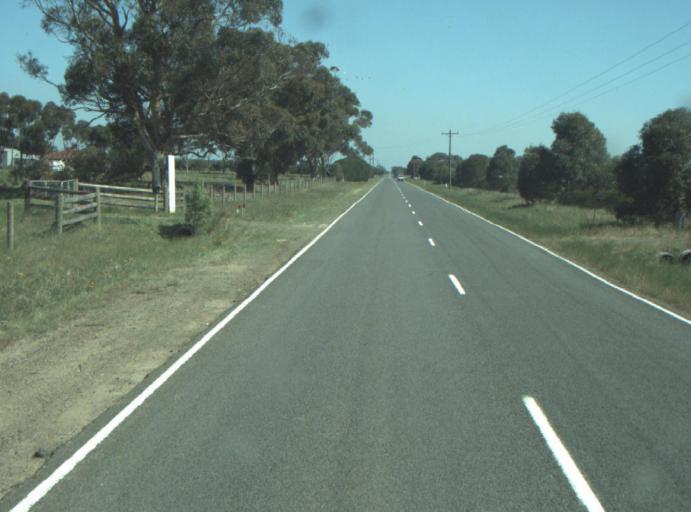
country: AU
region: Victoria
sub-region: Greater Geelong
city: Lara
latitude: -37.9762
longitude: 144.4047
